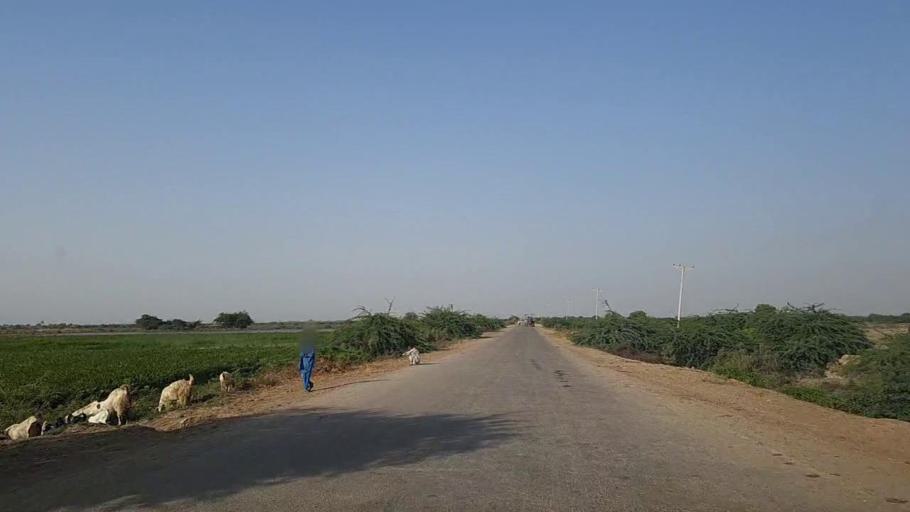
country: PK
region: Sindh
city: Mirpur Batoro
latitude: 24.5994
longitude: 68.4004
